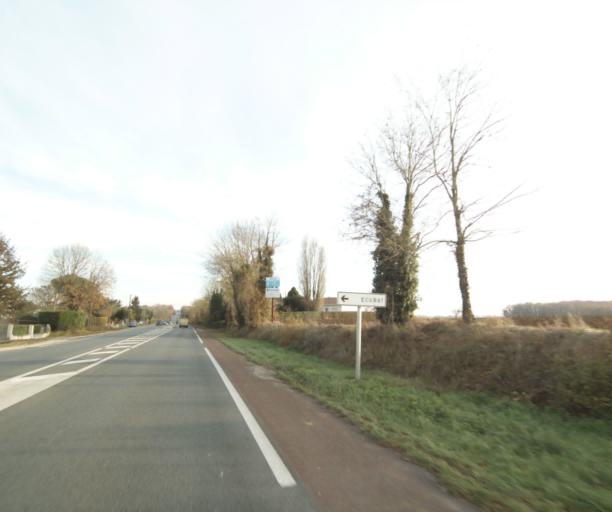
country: FR
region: Poitou-Charentes
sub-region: Departement de la Charente-Maritime
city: Saint-Georges-des-Coteaux
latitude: 45.7658
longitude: -0.6776
